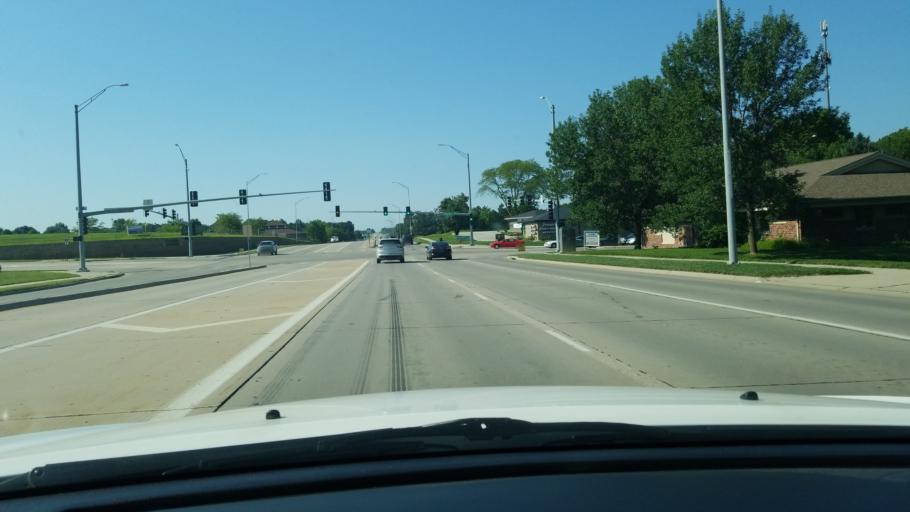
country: US
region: Nebraska
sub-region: Lancaster County
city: Lincoln
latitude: 40.7705
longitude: -96.6062
